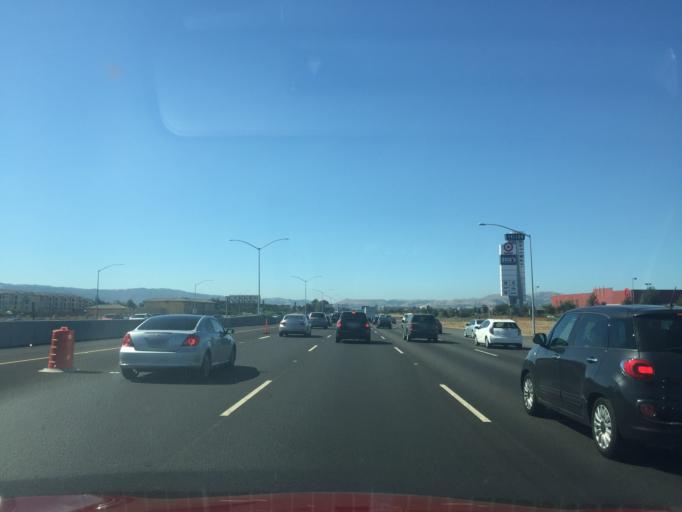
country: US
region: California
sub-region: Alameda County
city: Pleasanton
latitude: 37.7014
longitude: -121.8515
